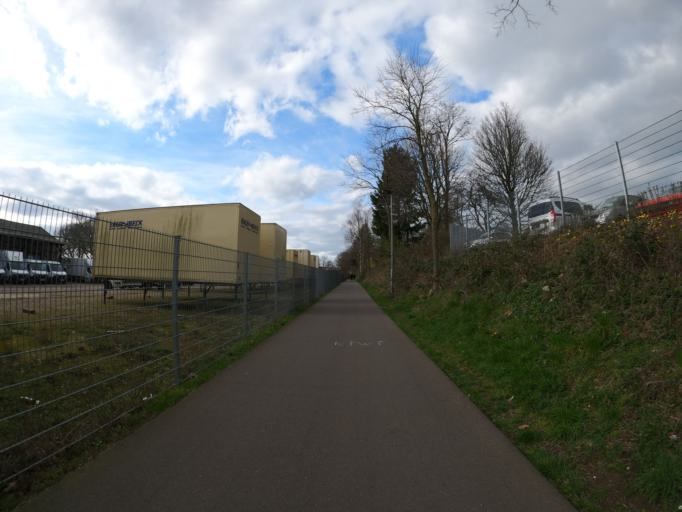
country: DE
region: North Rhine-Westphalia
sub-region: Regierungsbezirk Dusseldorf
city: Solingen
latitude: 51.1880
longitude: 7.0531
